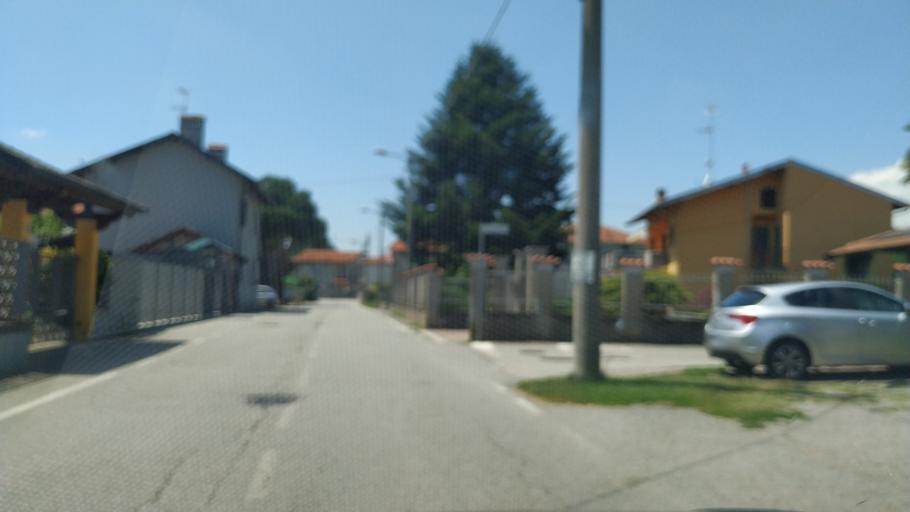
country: IT
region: Piedmont
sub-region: Provincia di Novara
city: Cureggio
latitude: 45.6775
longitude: 8.4610
